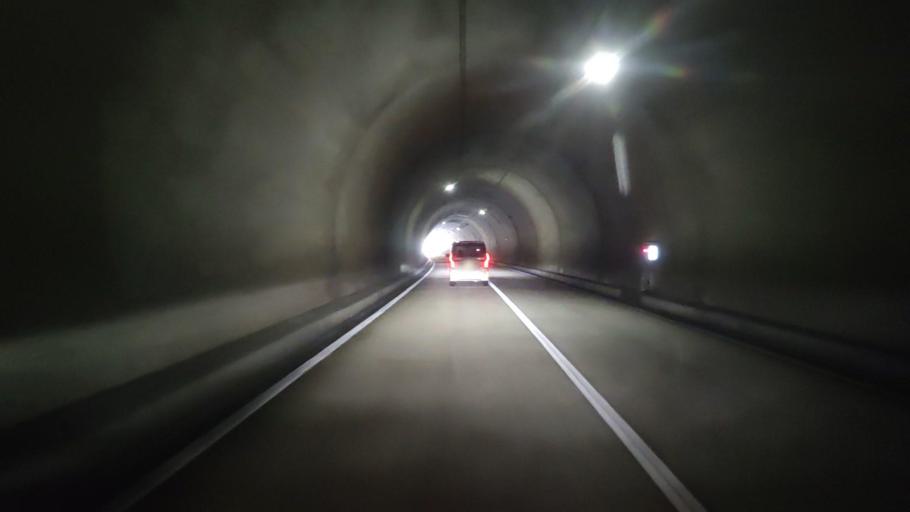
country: JP
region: Wakayama
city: Shingu
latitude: 33.8870
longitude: 135.8795
